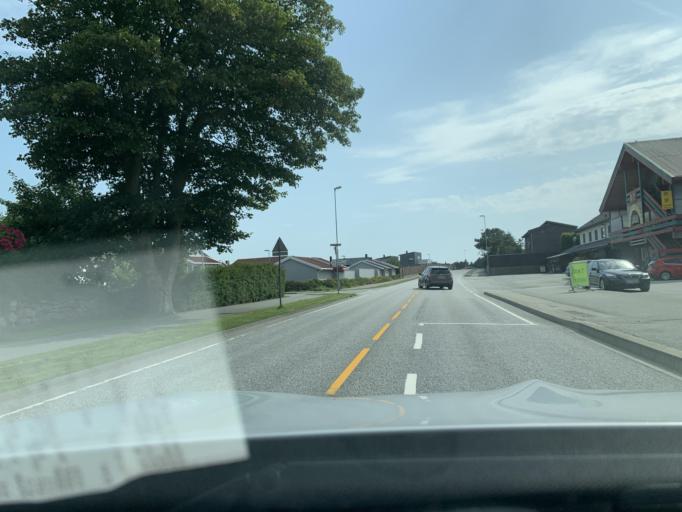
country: NO
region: Rogaland
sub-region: Klepp
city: Kleppe
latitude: 58.7703
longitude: 5.6298
